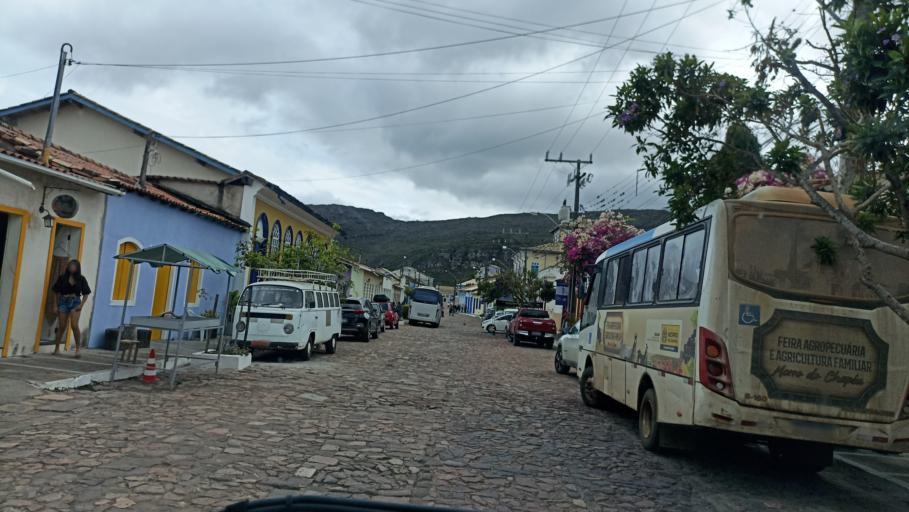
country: BR
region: Bahia
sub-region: Andarai
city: Vera Cruz
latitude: -13.0050
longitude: -41.3688
